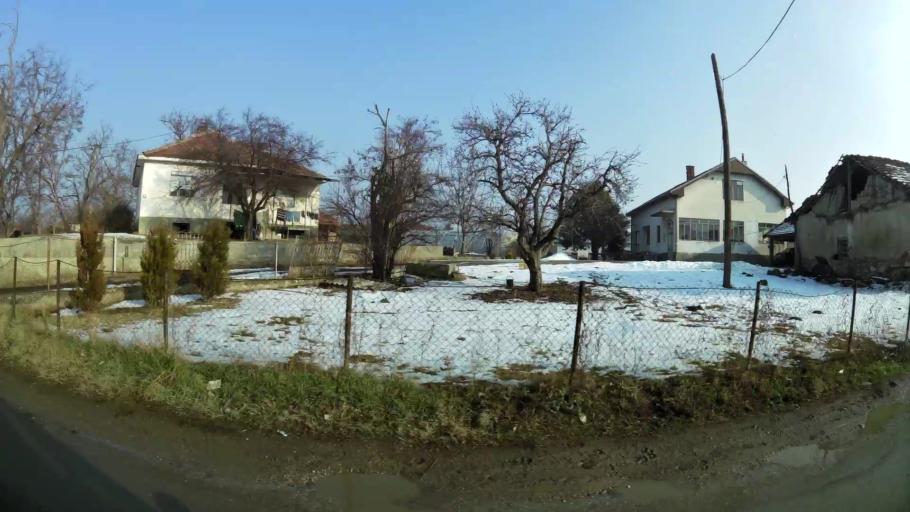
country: MK
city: Kadino
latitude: 41.9564
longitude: 21.6020
